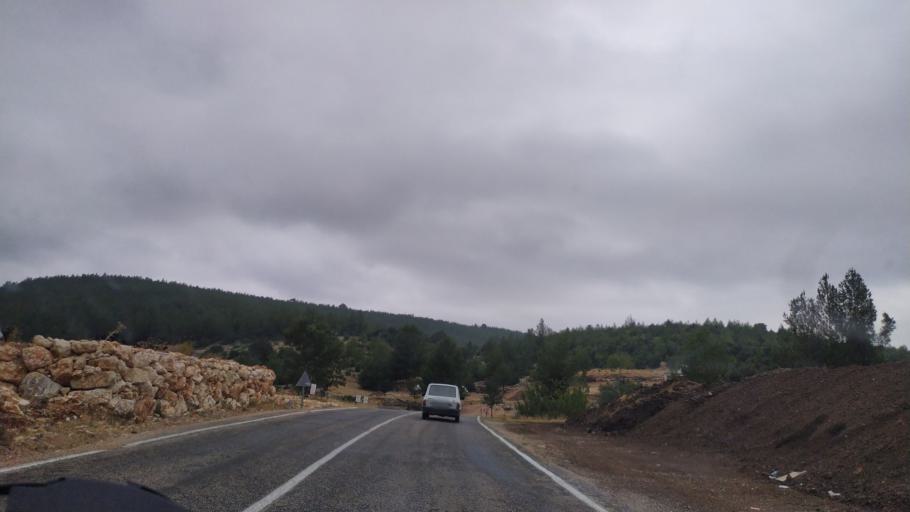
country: TR
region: Mersin
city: Silifke
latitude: 36.5409
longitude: 33.9364
